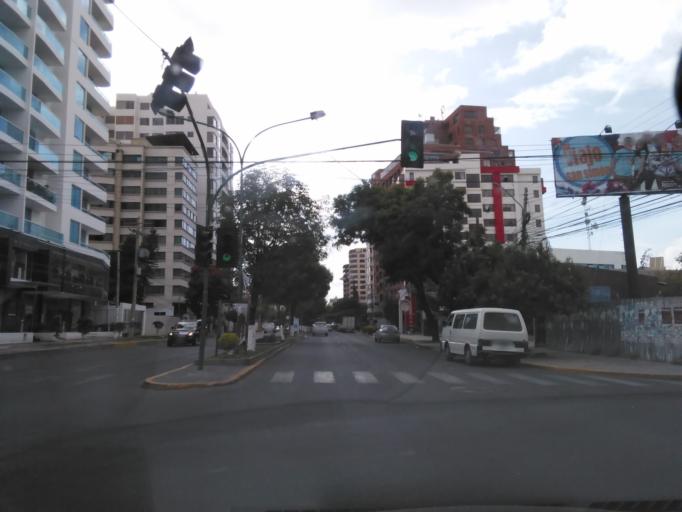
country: BO
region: Cochabamba
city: Cochabamba
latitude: -17.3728
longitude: -66.1591
